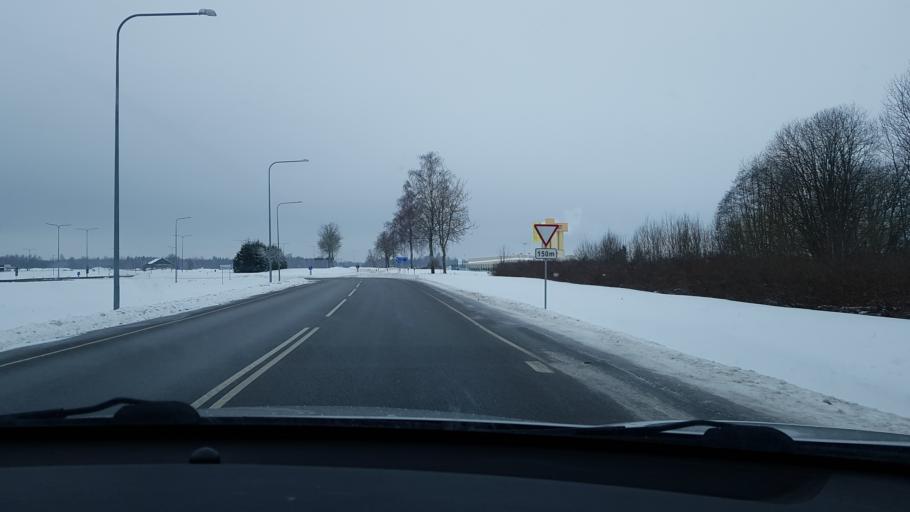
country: EE
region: Jaervamaa
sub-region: Paide linn
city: Paide
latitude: 58.9175
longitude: 25.6096
